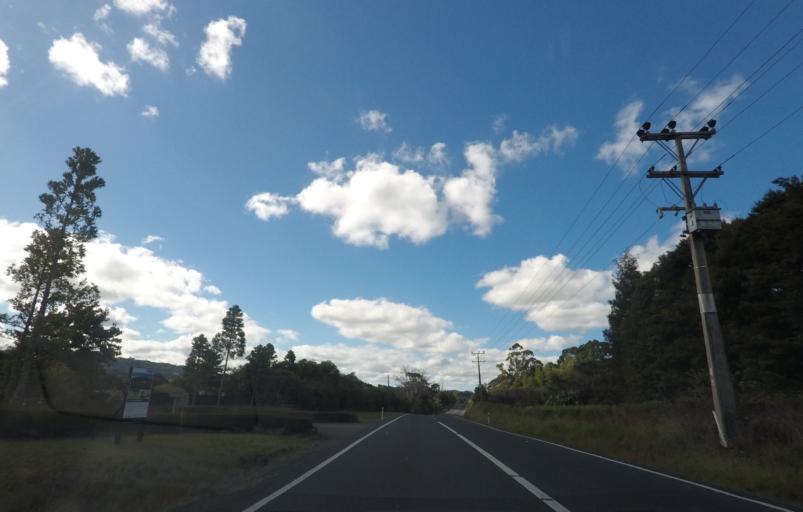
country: NZ
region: Auckland
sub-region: Auckland
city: Parakai
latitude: -36.6259
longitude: 174.5582
